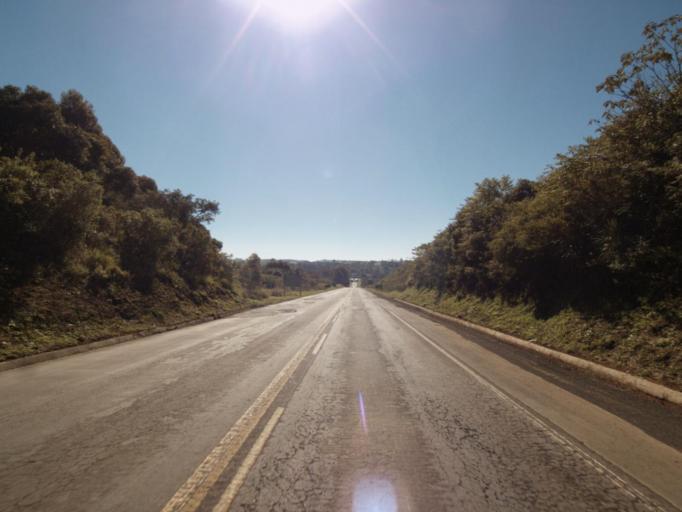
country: BR
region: Santa Catarina
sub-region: Sao Lourenco Do Oeste
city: Sao Lourenco dOeste
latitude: -26.8144
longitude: -53.1825
